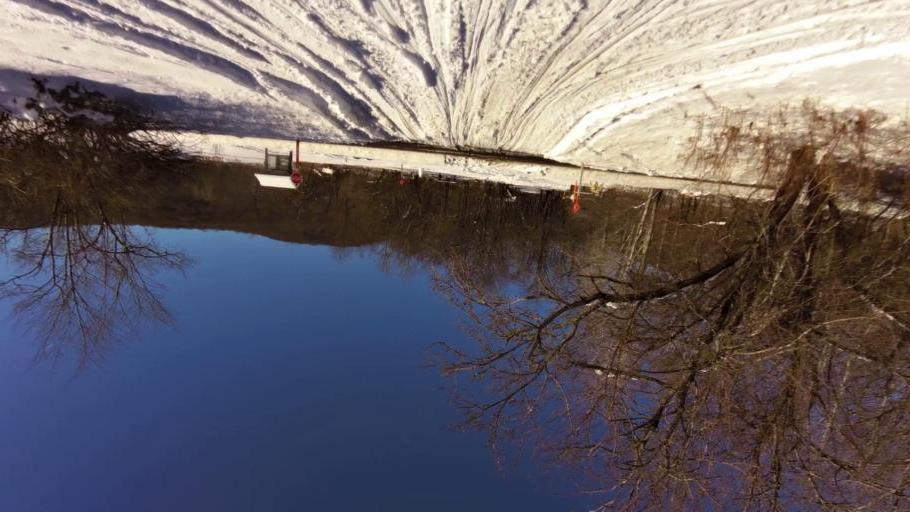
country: US
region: New York
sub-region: Cattaraugus County
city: Salamanca
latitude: 42.0738
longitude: -78.7108
